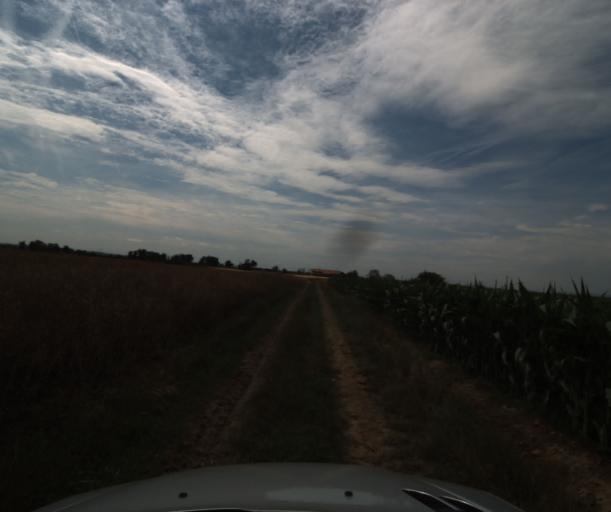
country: FR
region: Midi-Pyrenees
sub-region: Departement de la Haute-Garonne
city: Lacasse
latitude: 43.4156
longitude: 1.2626
